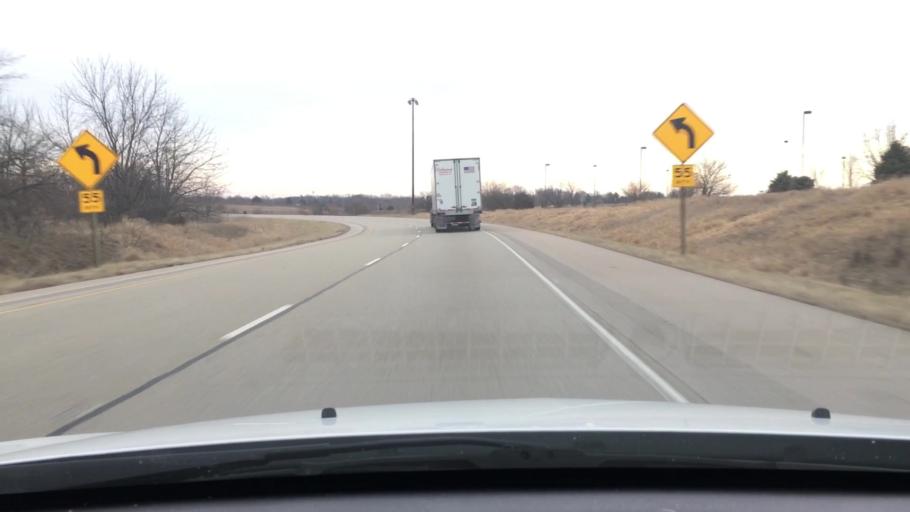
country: US
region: Illinois
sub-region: McLean County
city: Normal
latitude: 40.5369
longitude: -89.0120
